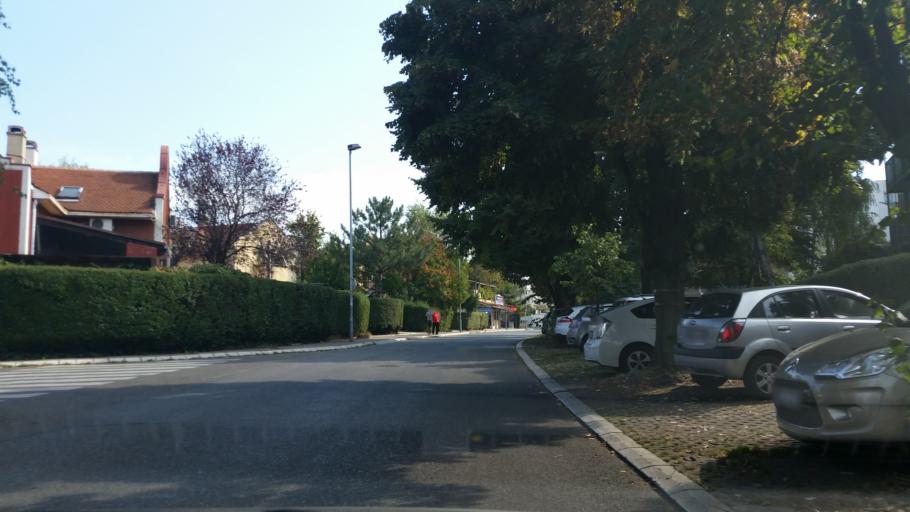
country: RS
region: Central Serbia
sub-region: Belgrade
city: Zemun
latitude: 44.8213
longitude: 20.3904
